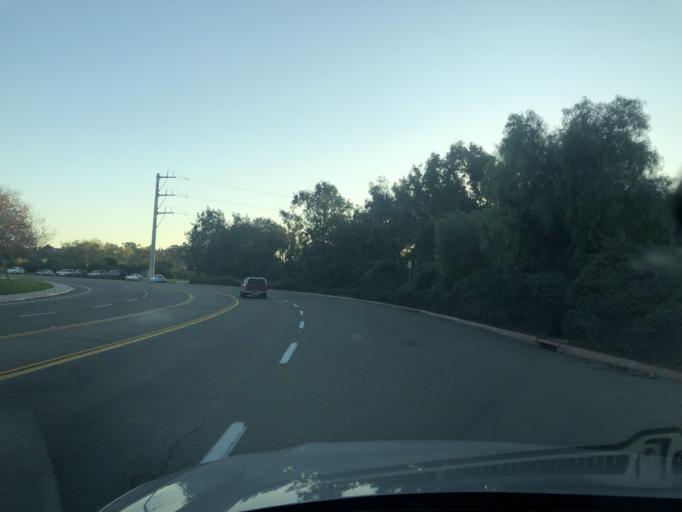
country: US
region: California
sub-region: San Diego County
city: Chula Vista
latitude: 32.6587
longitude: -117.0690
